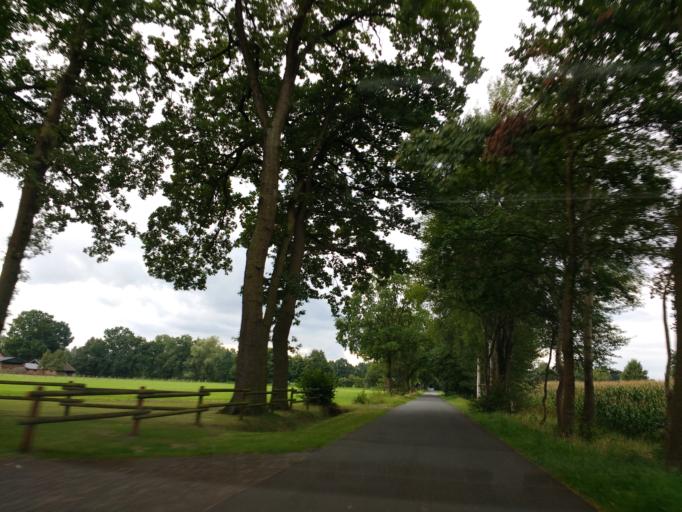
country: DE
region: North Rhine-Westphalia
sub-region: Regierungsbezirk Detmold
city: Hovelhof
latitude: 51.7703
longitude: 8.6552
